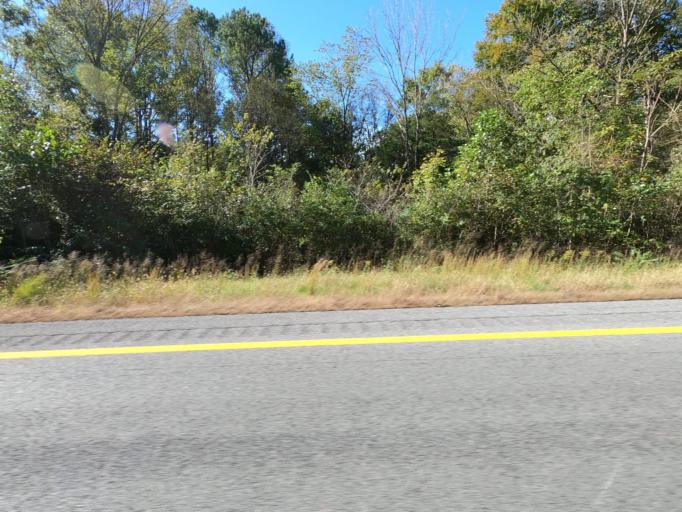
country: US
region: Tennessee
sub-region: Cheatham County
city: Pegram
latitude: 36.0792
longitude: -87.0371
